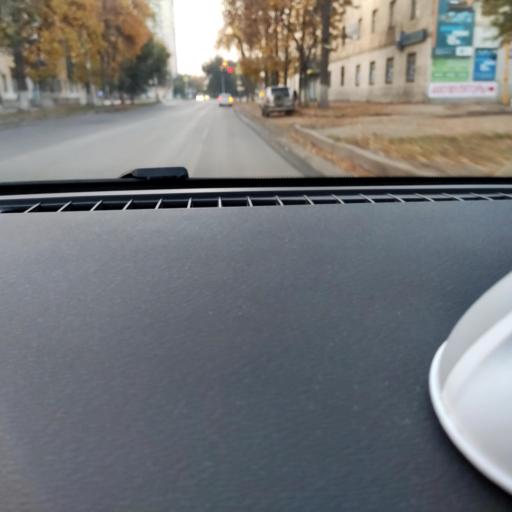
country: RU
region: Samara
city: Samara
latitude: 53.2016
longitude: 50.1781
